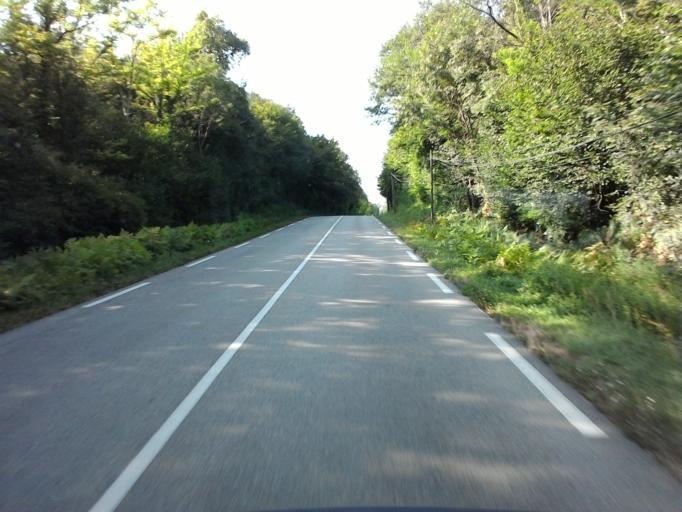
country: FR
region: Rhone-Alpes
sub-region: Departement de l'Isere
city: Bouvesse-Quirieu
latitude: 45.7732
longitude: 5.4013
